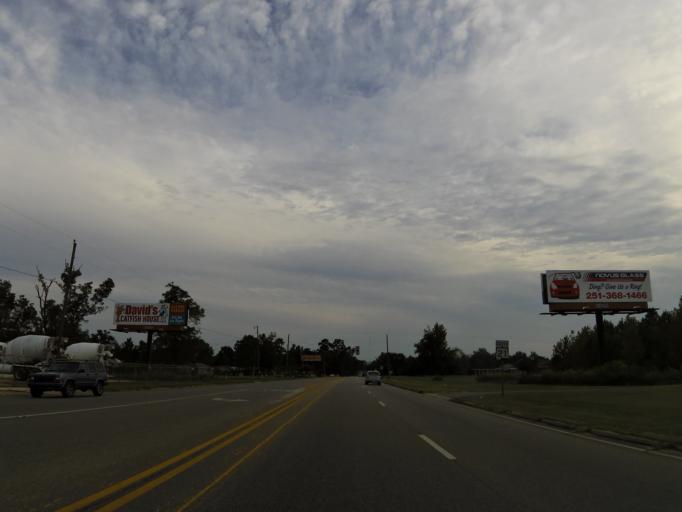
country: US
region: Alabama
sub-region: Escambia County
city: Atmore
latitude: 31.0485
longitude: -87.4931
